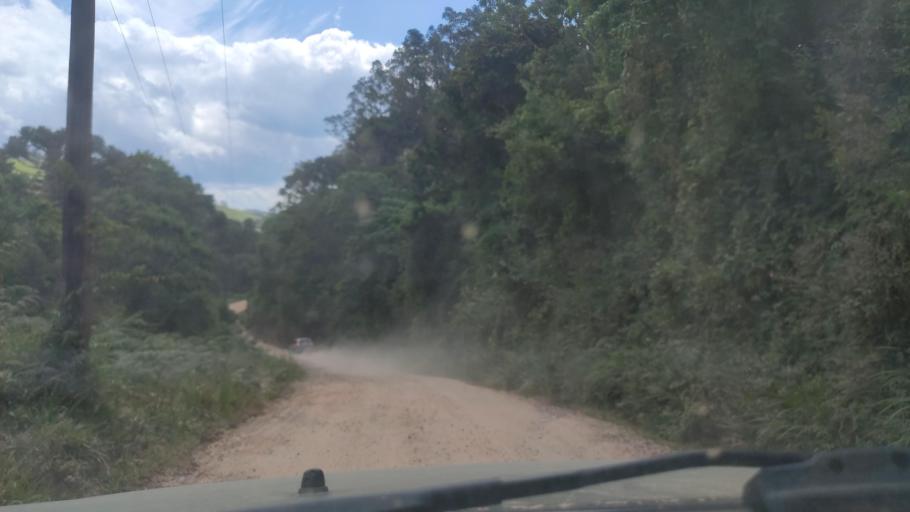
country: BR
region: Minas Gerais
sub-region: Cambui
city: Cambui
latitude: -22.7042
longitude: -46.0172
